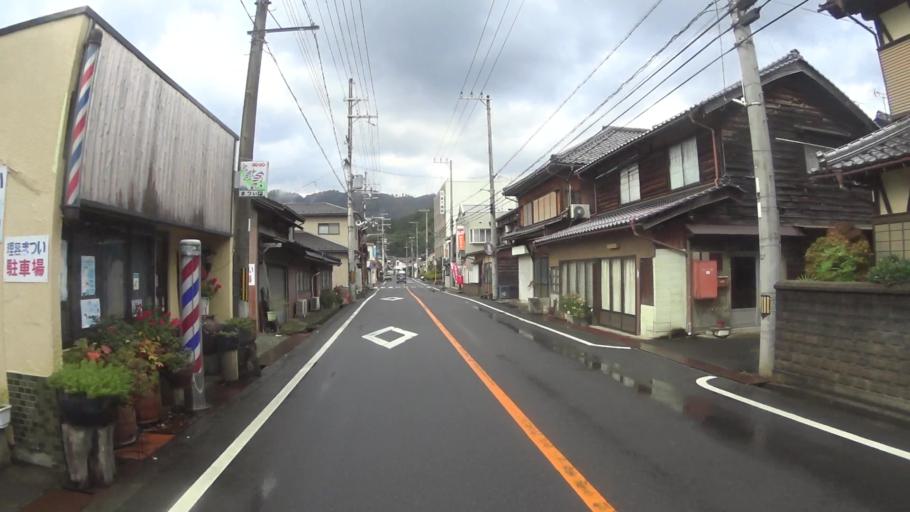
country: JP
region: Kyoto
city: Miyazu
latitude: 35.5511
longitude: 135.1525
